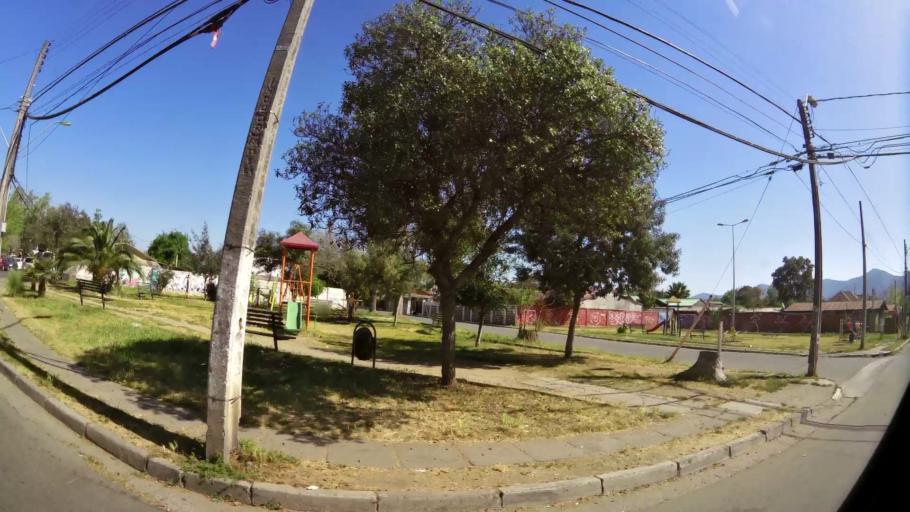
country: CL
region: Santiago Metropolitan
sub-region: Provincia de Talagante
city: Penaflor
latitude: -33.6046
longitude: -70.8922
